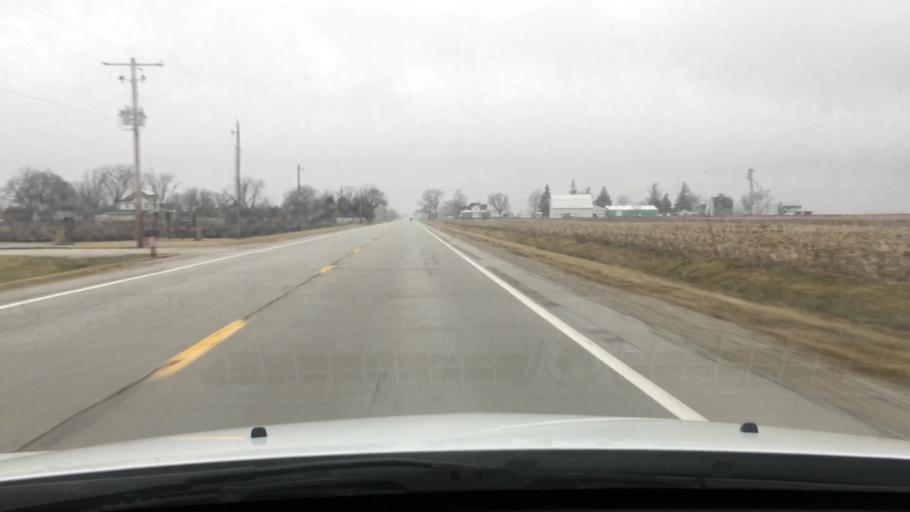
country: US
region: Illinois
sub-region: Livingston County
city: Flanagan
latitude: 40.8706
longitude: -88.8781
